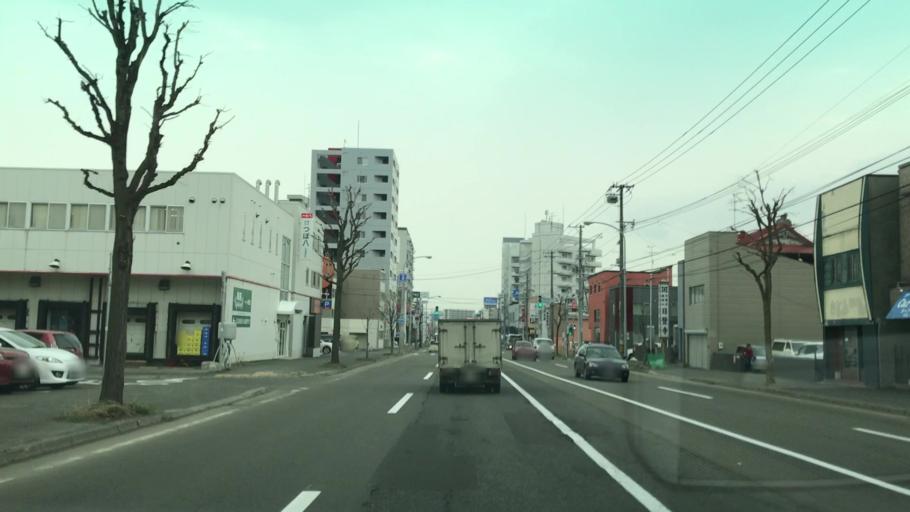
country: JP
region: Hokkaido
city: Sapporo
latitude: 43.0713
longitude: 141.3025
